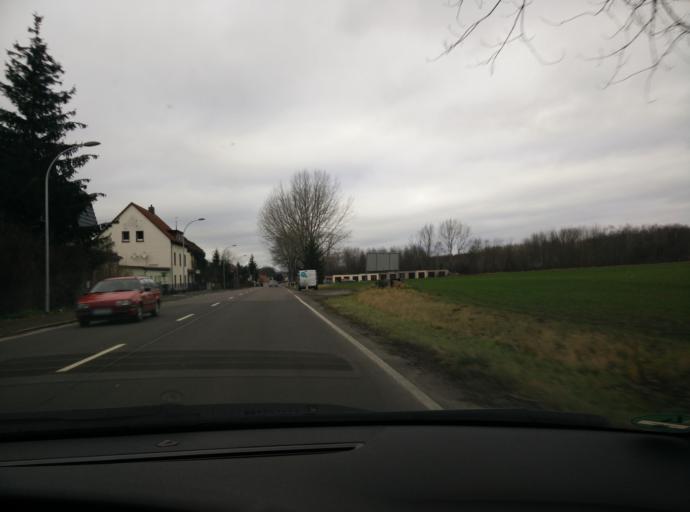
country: DE
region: Saxony
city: Borna
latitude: 51.1004
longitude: 12.5190
